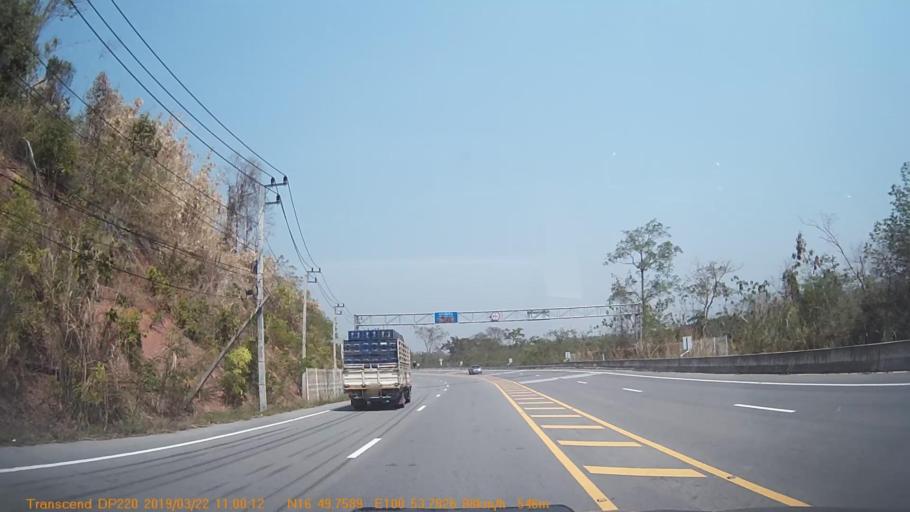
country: TH
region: Phetchabun
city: Khao Kho
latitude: 16.8293
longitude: 100.8962
